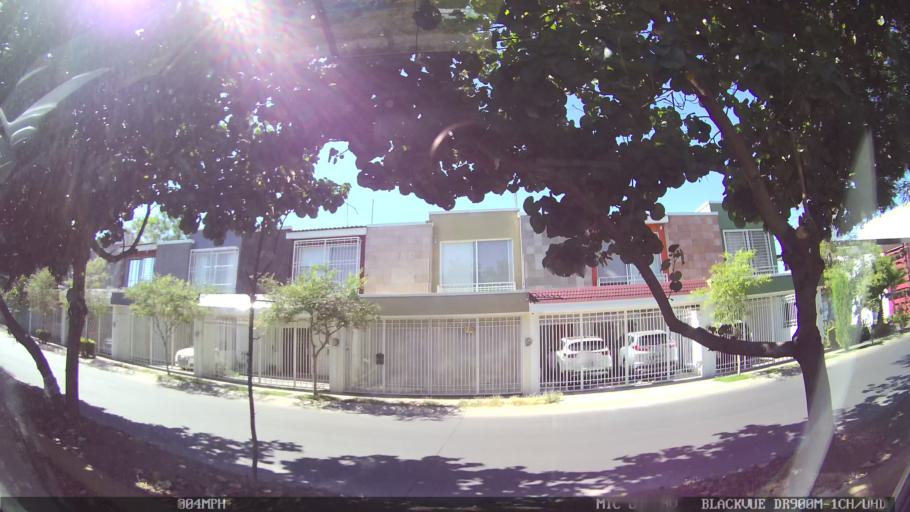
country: MX
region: Jalisco
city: Tlaquepaque
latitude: 20.6478
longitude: -103.2914
